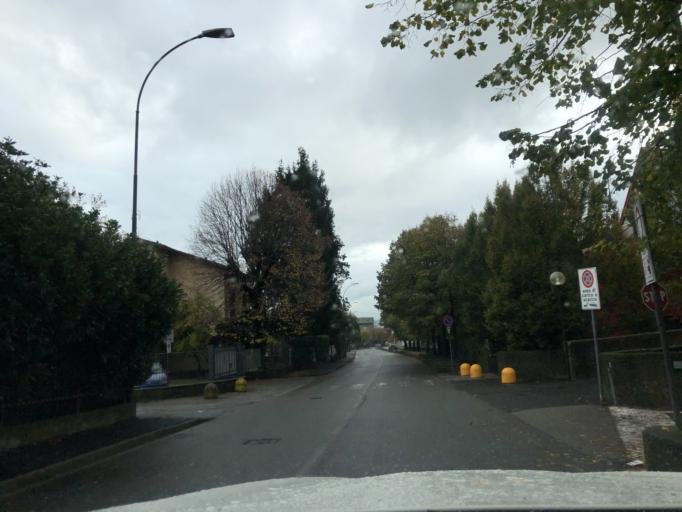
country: IT
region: Lombardy
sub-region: Provincia di Como
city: Erba
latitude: 45.8052
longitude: 9.2212
